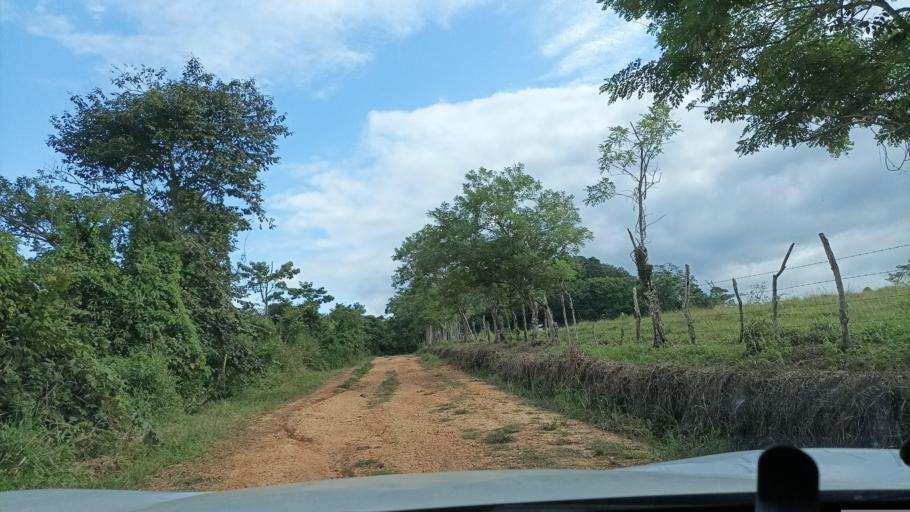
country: MX
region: Veracruz
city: Soconusco
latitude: 17.9441
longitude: -94.8826
